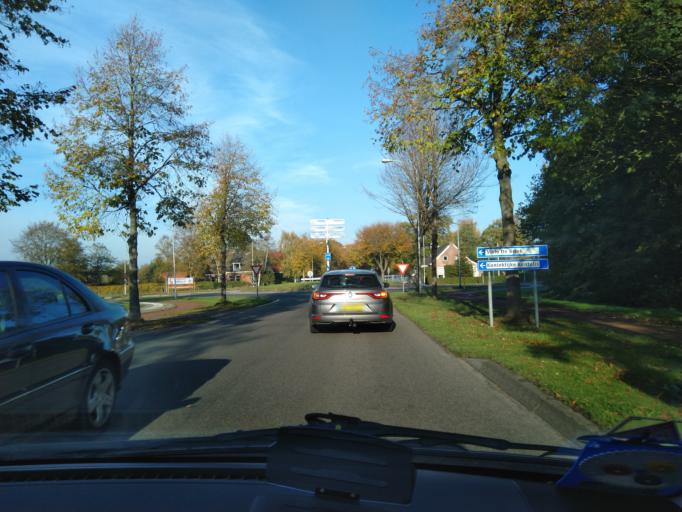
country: NL
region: Drenthe
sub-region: Gemeente Tynaarlo
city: Vries
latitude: 53.0803
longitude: 6.5806
